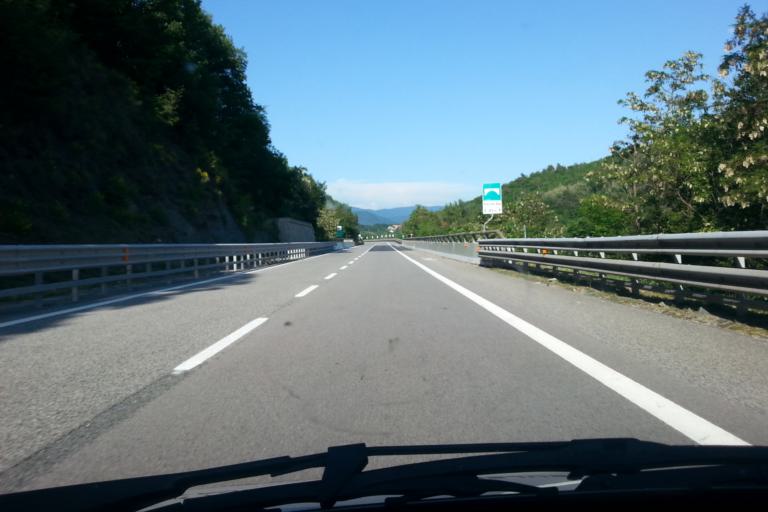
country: IT
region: Liguria
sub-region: Provincia di Savona
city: Plodio
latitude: 44.3651
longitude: 8.2491
